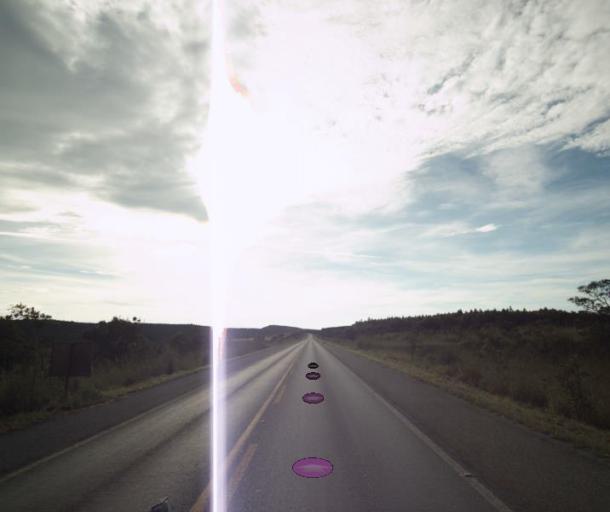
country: BR
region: Goias
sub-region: Pirenopolis
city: Pirenopolis
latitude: -15.7507
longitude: -48.6194
